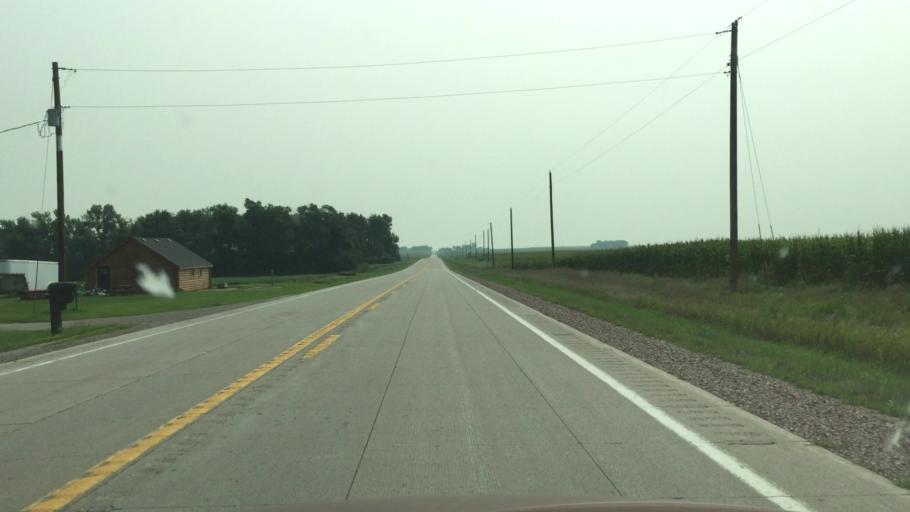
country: US
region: Iowa
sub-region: Osceola County
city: Sibley
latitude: 43.4327
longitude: -95.6957
